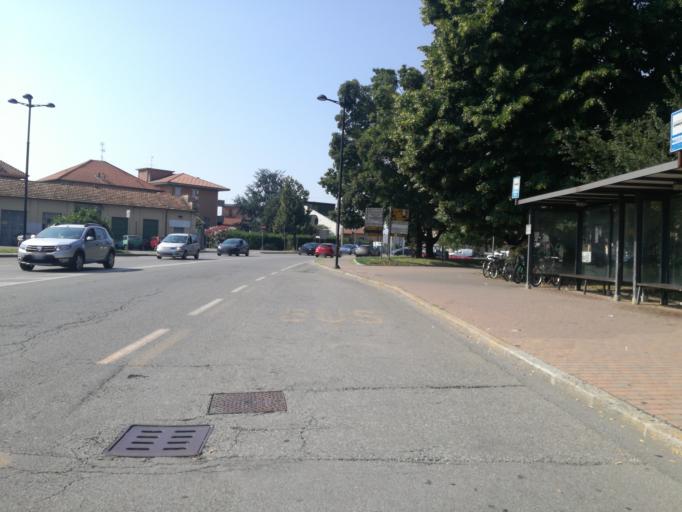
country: IT
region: Lombardy
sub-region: Citta metropolitana di Milano
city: Trezzo sull'Adda
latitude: 45.6077
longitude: 9.5209
